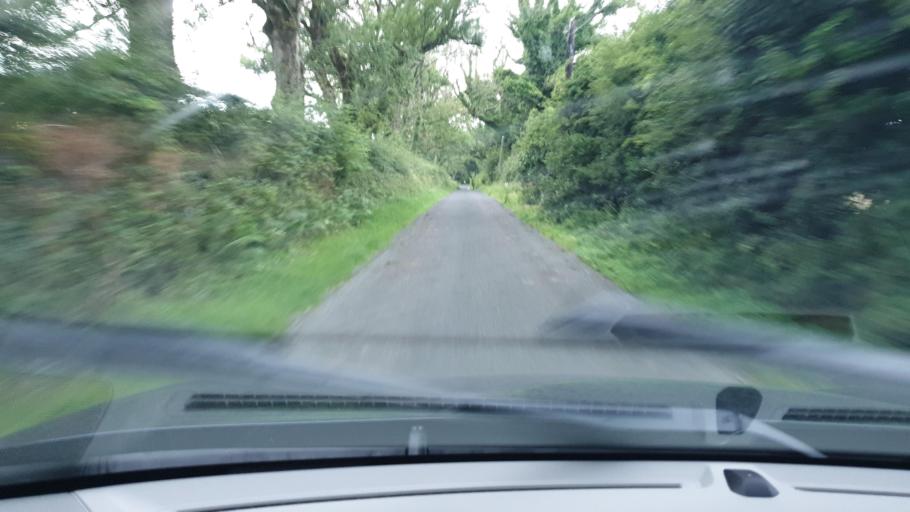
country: IE
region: Leinster
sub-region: Wicklow
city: Blessington
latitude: 53.2280
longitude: -6.5147
